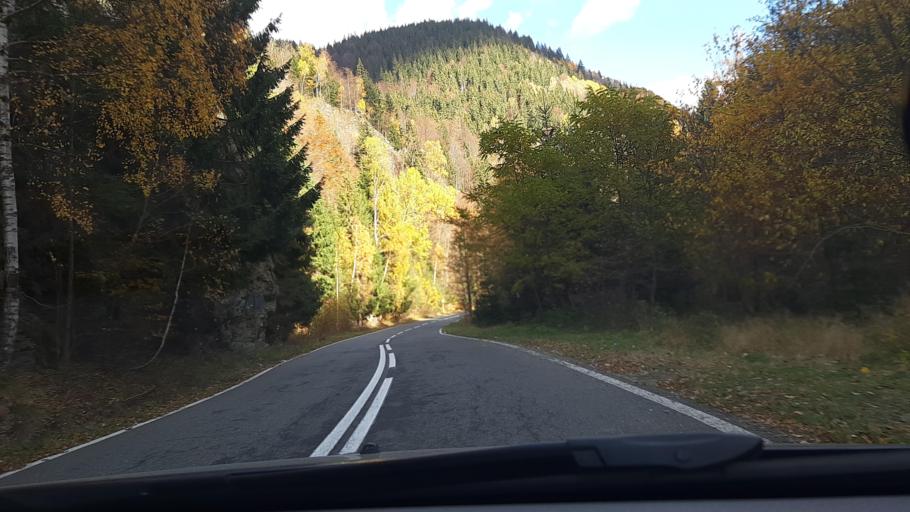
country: RO
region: Valcea
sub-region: Comuna Voineasa
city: Voineasa
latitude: 45.4368
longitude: 23.8587
